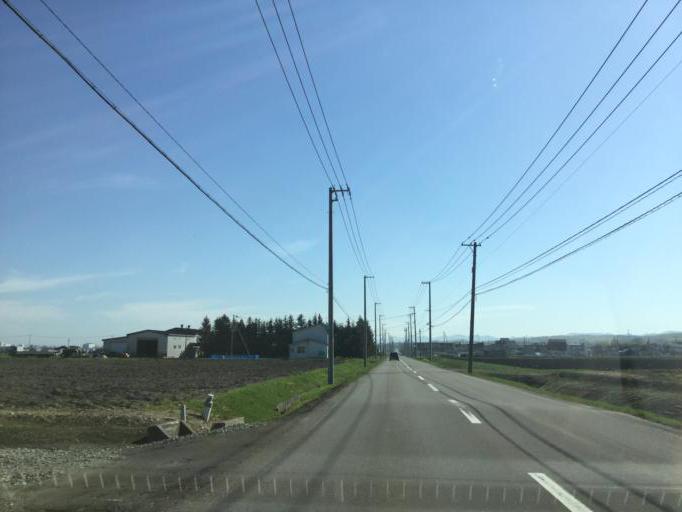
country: JP
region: Hokkaido
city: Iwamizawa
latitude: 43.1737
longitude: 141.7480
